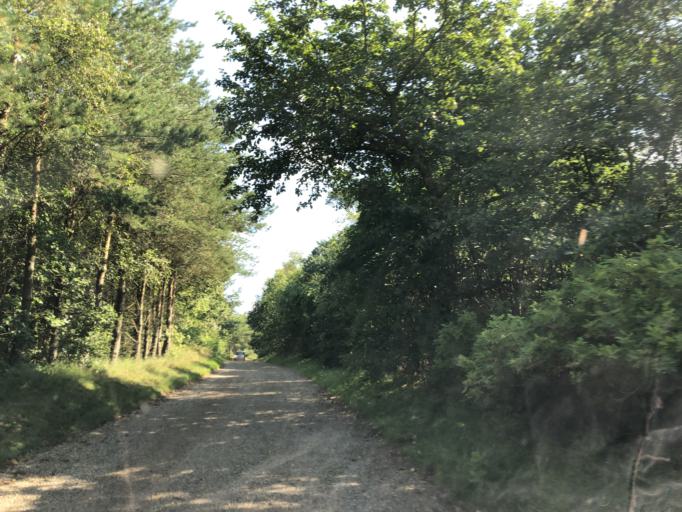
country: DK
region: Central Jutland
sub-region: Skive Kommune
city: Skive
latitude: 56.5233
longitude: 8.9604
